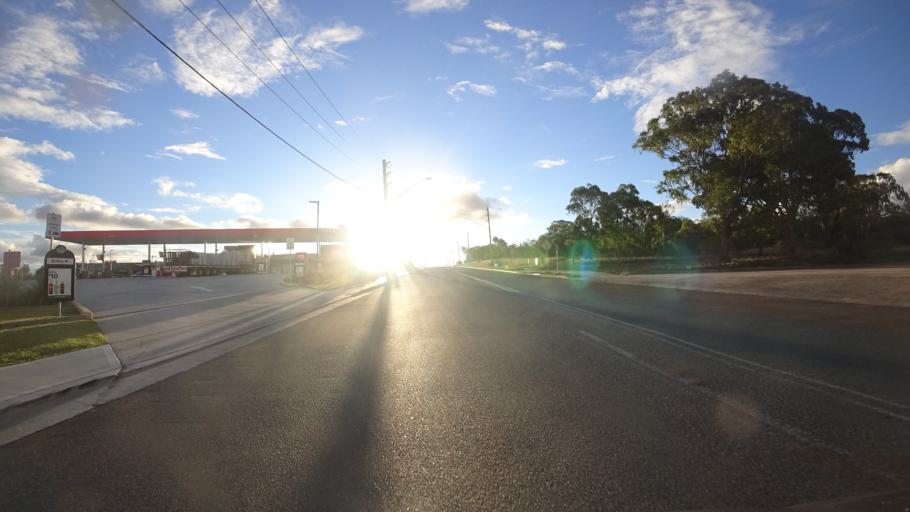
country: AU
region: New South Wales
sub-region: Goulburn Mulwaree
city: Goulburn
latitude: -34.7722
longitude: 149.6907
